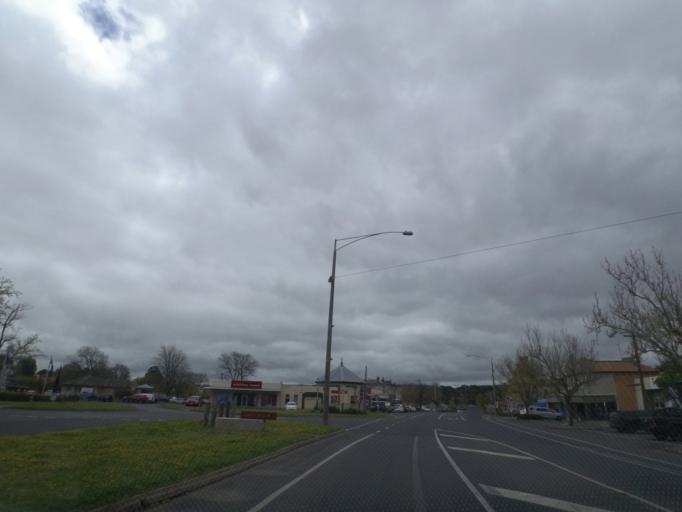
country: AU
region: Victoria
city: Brown Hill
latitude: -37.4251
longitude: 143.8941
